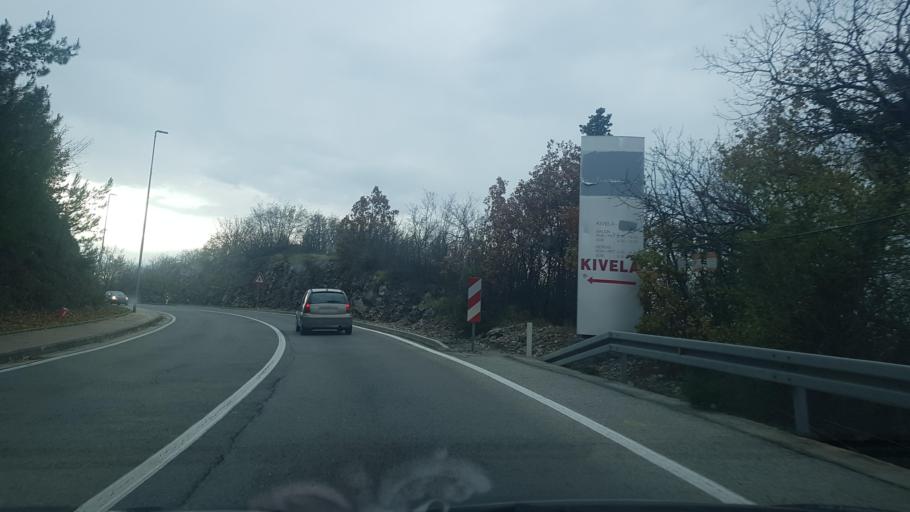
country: HR
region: Primorsko-Goranska
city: Cernik
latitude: 45.3120
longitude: 14.4817
